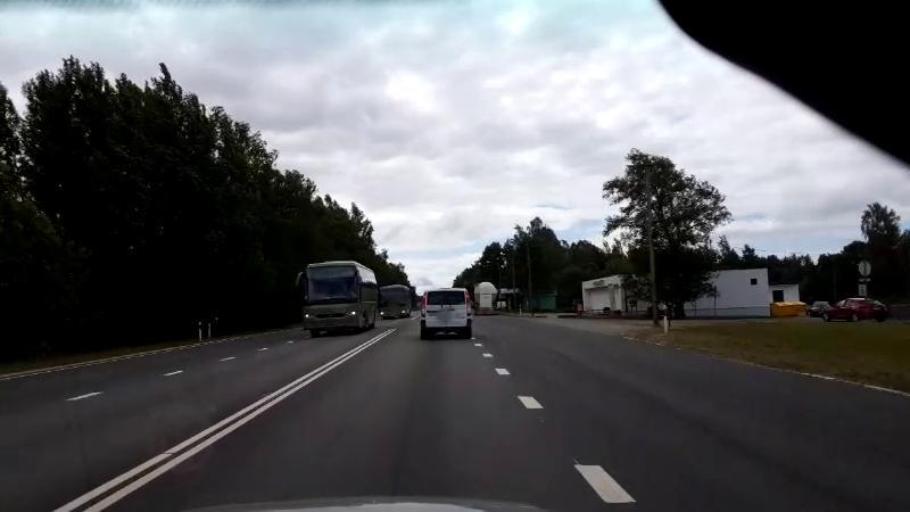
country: EE
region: Paernumaa
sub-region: Paernu linn
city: Parnu
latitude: 58.2038
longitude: 24.4854
